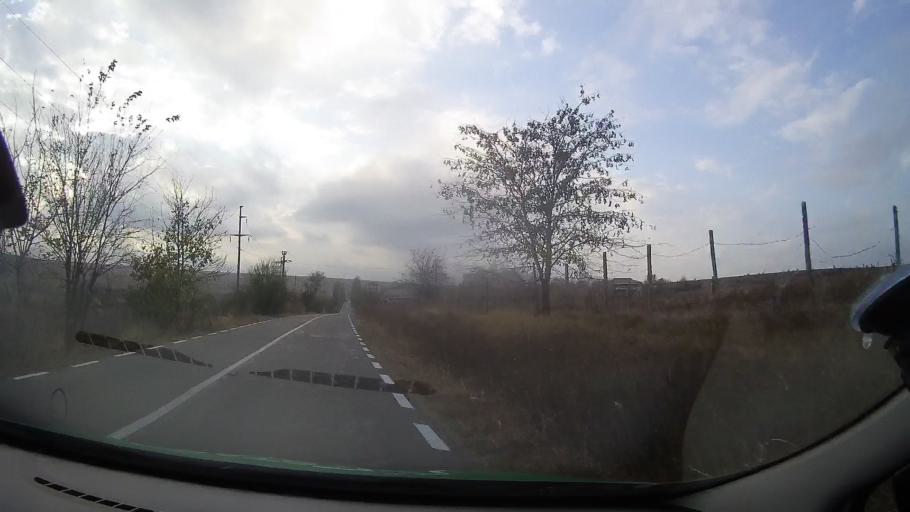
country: RO
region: Constanta
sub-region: Comuna Mircea Voda
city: Satu Nou
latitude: 44.2361
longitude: 28.2360
